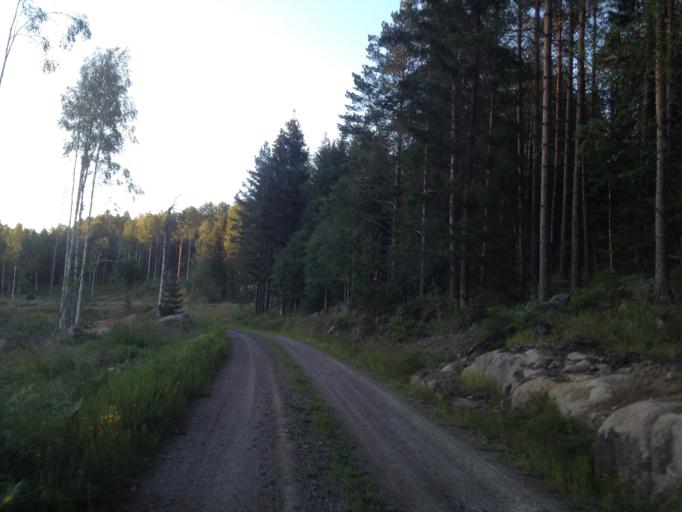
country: SE
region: Kalmar
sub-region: Vasterviks Kommun
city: Overum
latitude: 58.0068
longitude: 16.1222
